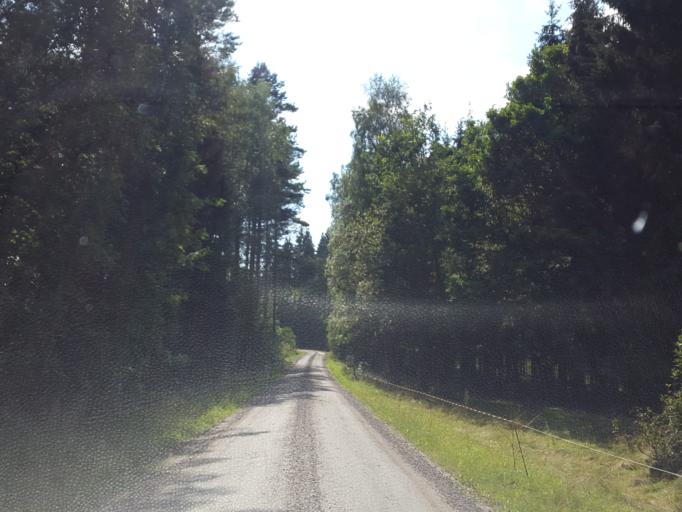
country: SE
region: Vaestra Goetaland
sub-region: Herrljunga Kommun
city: Herrljunga
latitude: 58.0302
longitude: 13.1326
